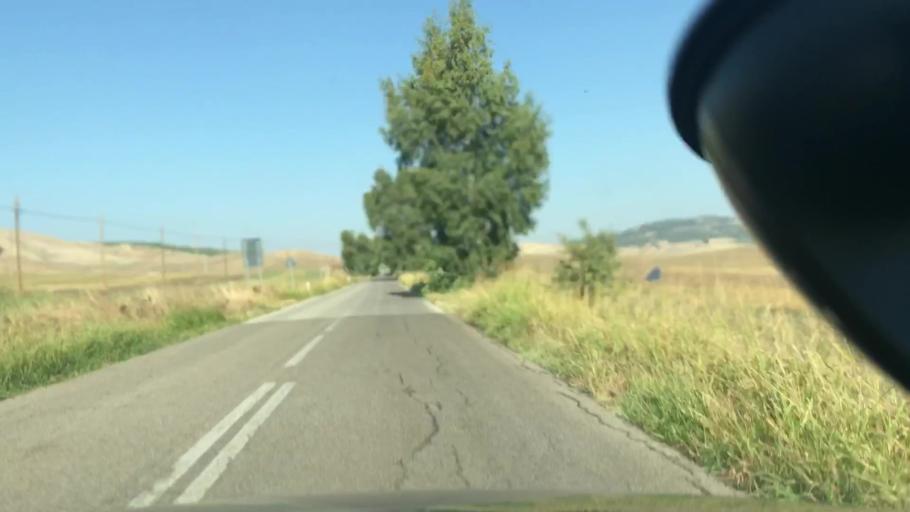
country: IT
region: Basilicate
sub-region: Provincia di Matera
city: La Martella
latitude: 40.6589
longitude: 16.5159
